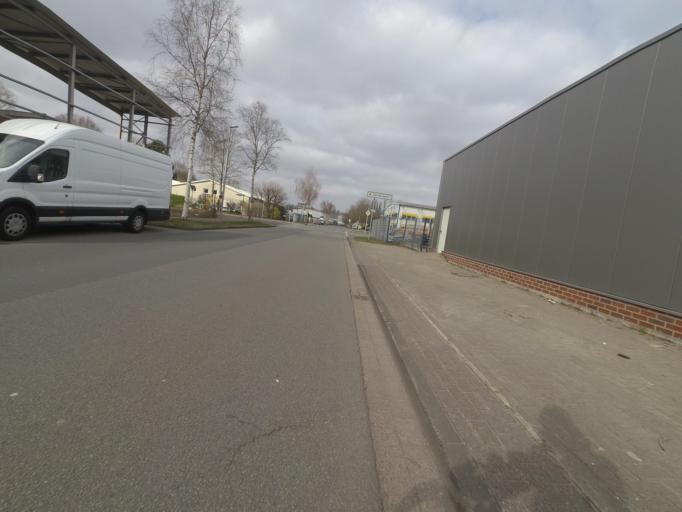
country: DE
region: Lower Saxony
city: Oldenburg
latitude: 53.1074
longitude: 8.2532
